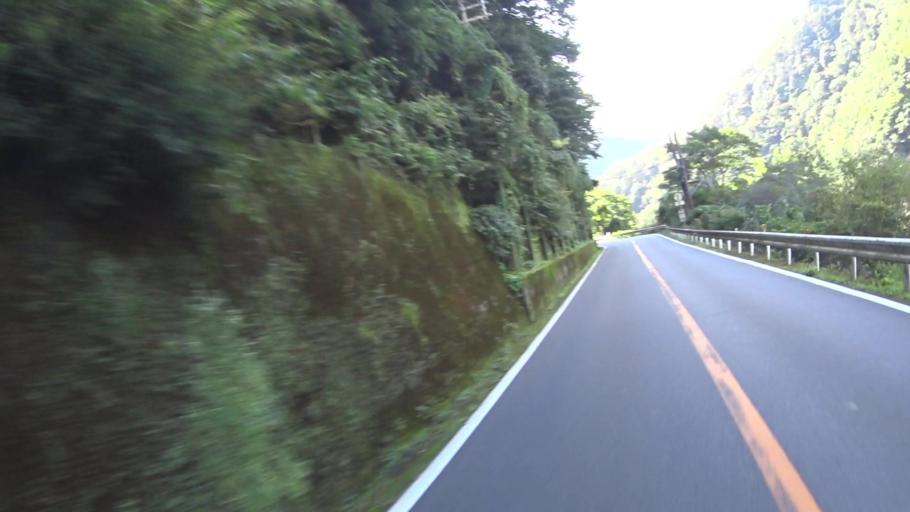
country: JP
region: Kyoto
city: Uji
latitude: 34.8690
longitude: 135.8415
